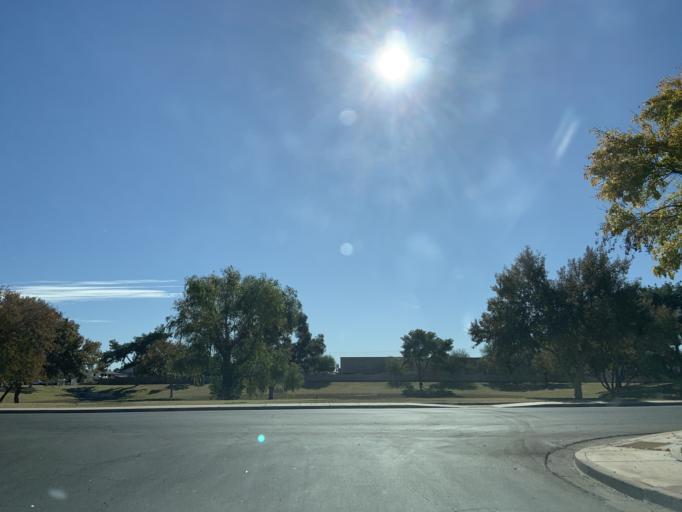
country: US
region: Arizona
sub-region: Maricopa County
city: San Carlos
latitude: 33.3673
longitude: -111.8576
